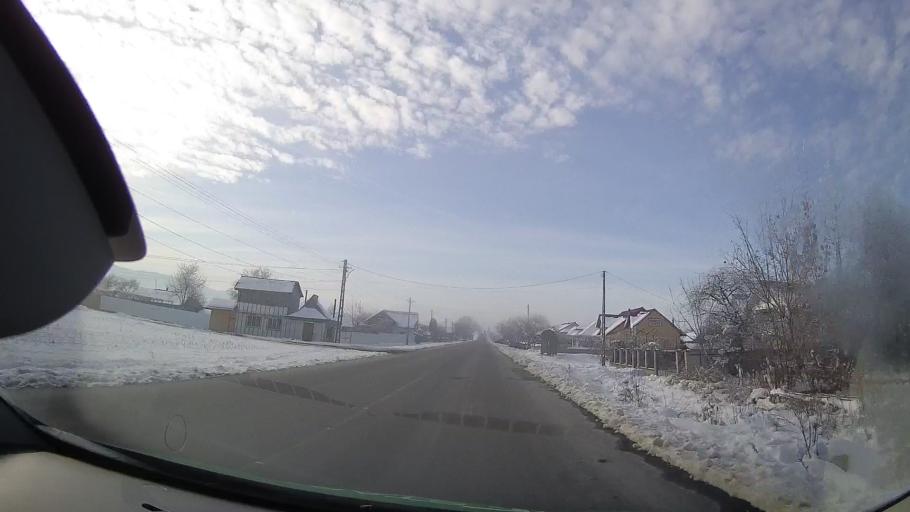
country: RO
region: Neamt
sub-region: Comuna Timisesti
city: Dumbrava
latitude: 47.2192
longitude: 26.4580
